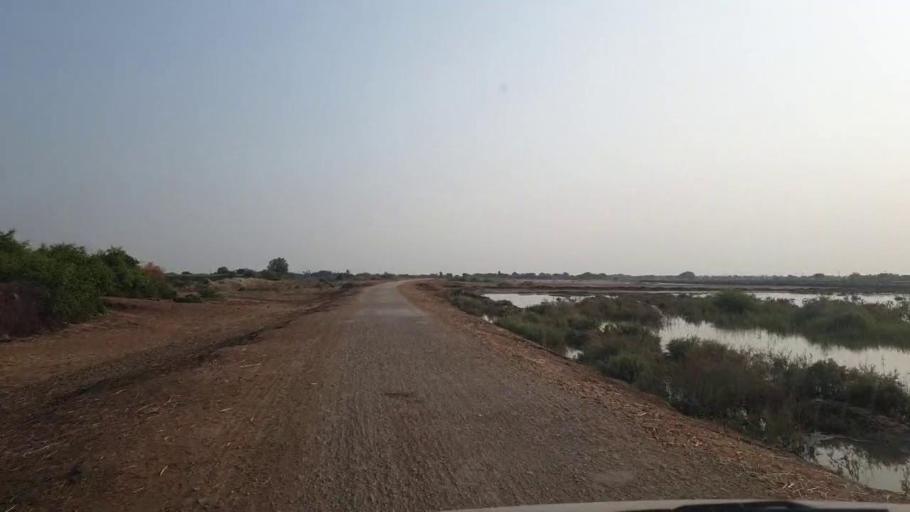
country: PK
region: Sindh
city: Rajo Khanani
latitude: 25.0472
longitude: 68.7661
